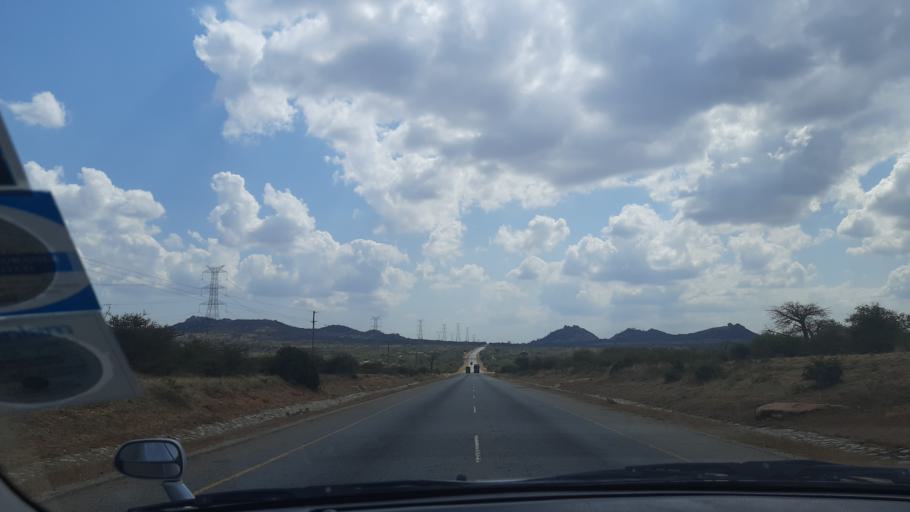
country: TZ
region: Dodoma
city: Dodoma
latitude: -6.0489
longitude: 35.5276
